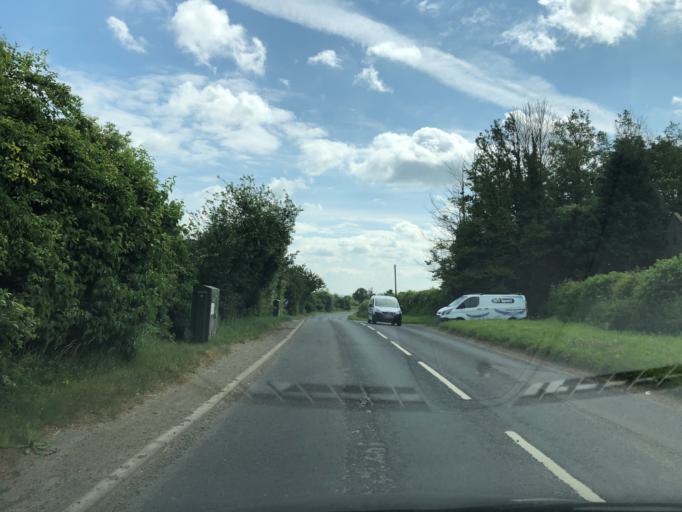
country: GB
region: England
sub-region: North Yorkshire
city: Helmsley
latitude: 54.1700
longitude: -0.9770
